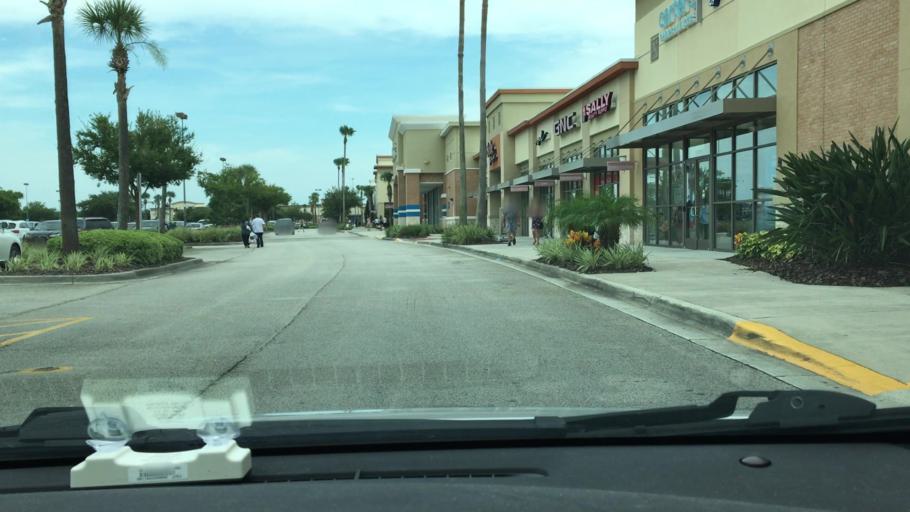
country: US
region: Florida
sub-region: Seminole County
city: Lake Mary
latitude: 28.7986
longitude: -81.3355
